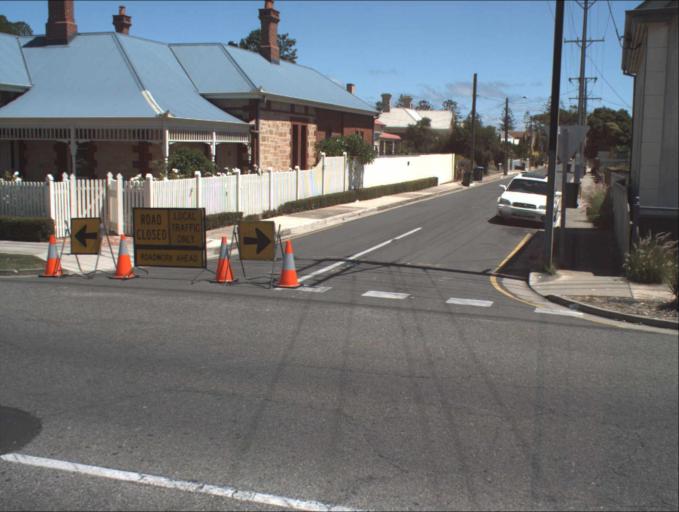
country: AU
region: South Australia
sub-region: Port Adelaide Enfield
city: Birkenhead
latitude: -34.8426
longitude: 138.4825
